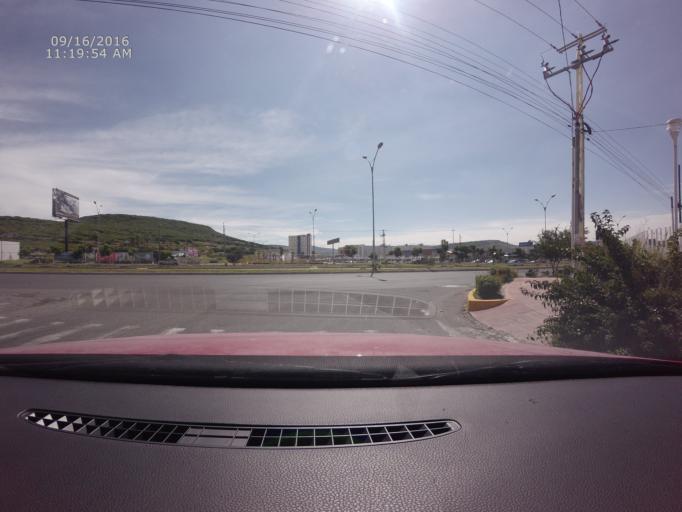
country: MX
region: Queretaro
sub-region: Queretaro
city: El Salitre
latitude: 20.6775
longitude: -100.4349
